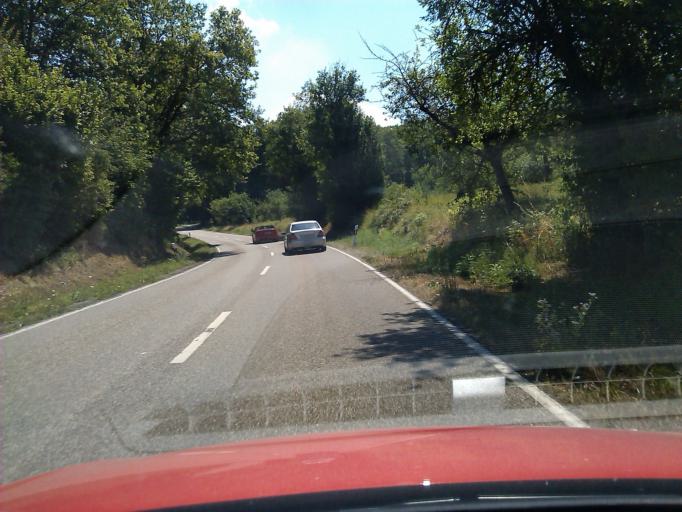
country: DE
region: Baden-Wuerttemberg
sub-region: Regierungsbezirk Stuttgart
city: Schwaigern
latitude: 49.1267
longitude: 9.0682
